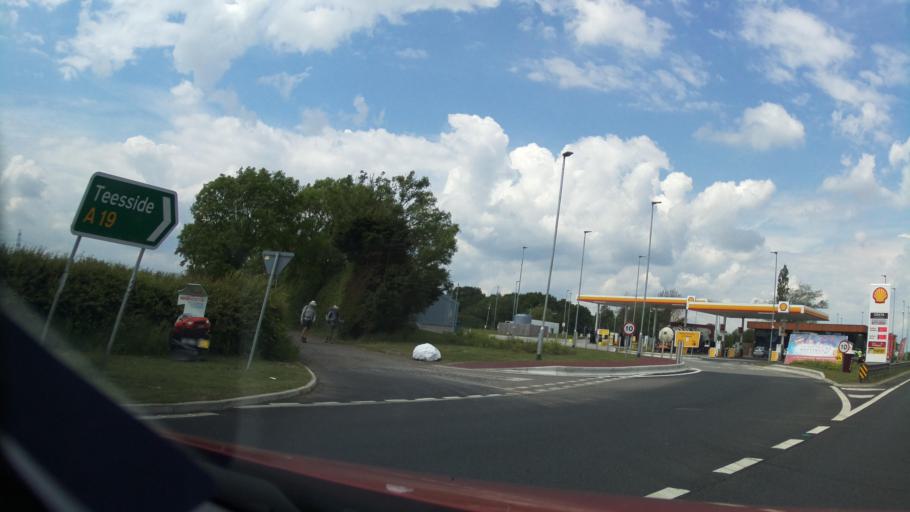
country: GB
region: England
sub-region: Stockton-on-Tees
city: Yarm
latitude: 54.4036
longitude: -1.3199
